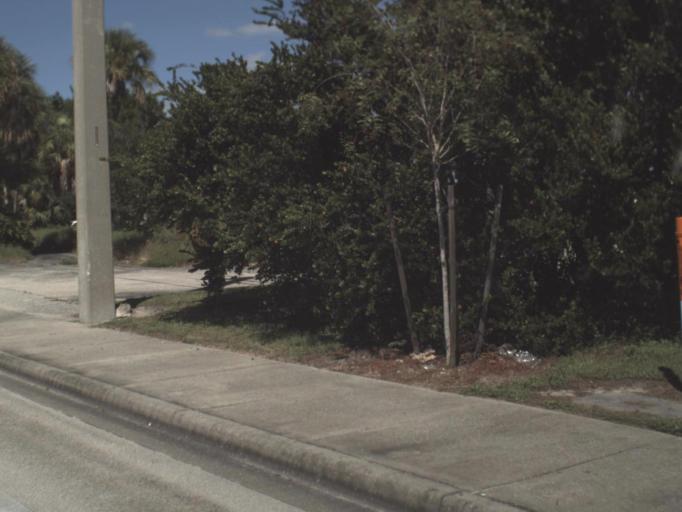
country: US
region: Florida
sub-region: Collier County
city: Naples
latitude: 26.1373
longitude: -81.7811
